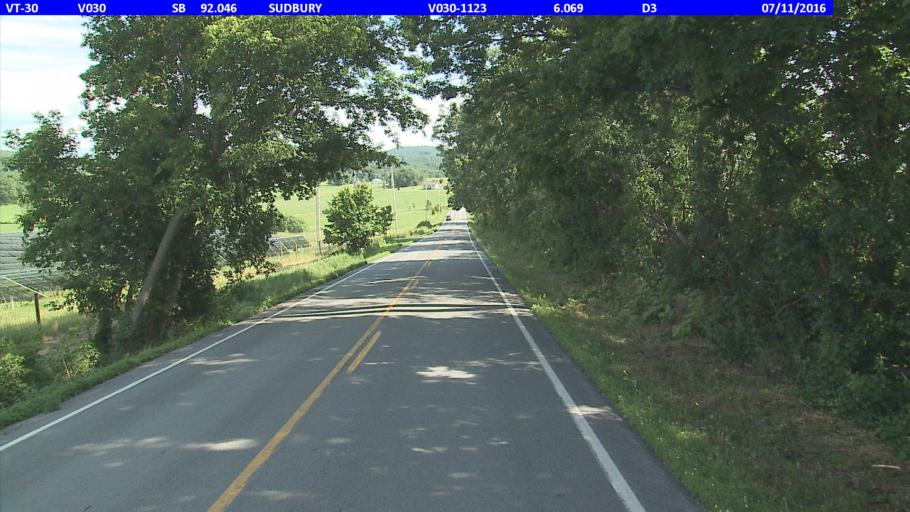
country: US
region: Vermont
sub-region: Rutland County
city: Brandon
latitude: 43.8336
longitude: -73.1940
